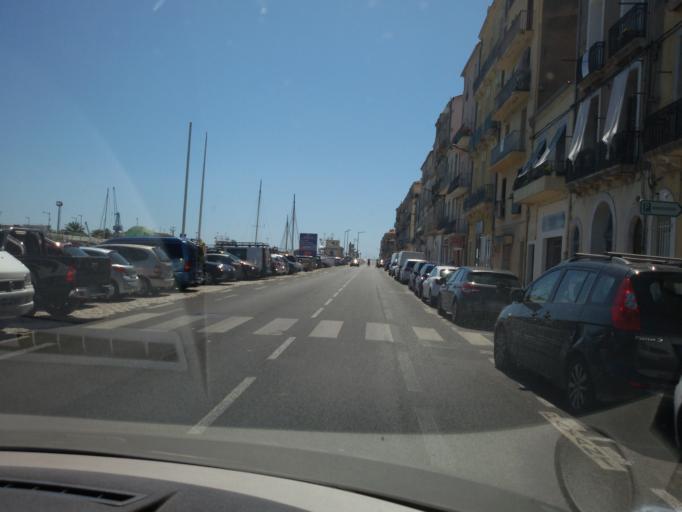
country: FR
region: Languedoc-Roussillon
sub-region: Departement de l'Herault
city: Sete
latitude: 43.4069
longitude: 3.7010
